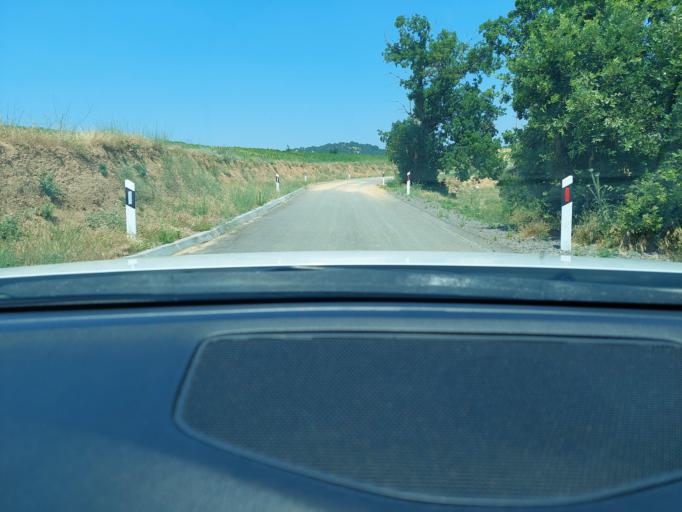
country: MK
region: Radovis
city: Radovish
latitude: 41.6614
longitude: 22.4102
